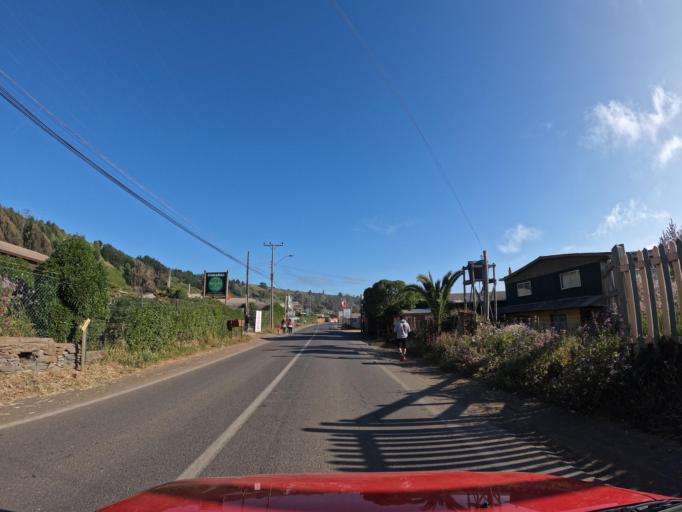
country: CL
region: Maule
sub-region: Provincia de Talca
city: Constitucion
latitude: -34.8985
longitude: -72.1794
